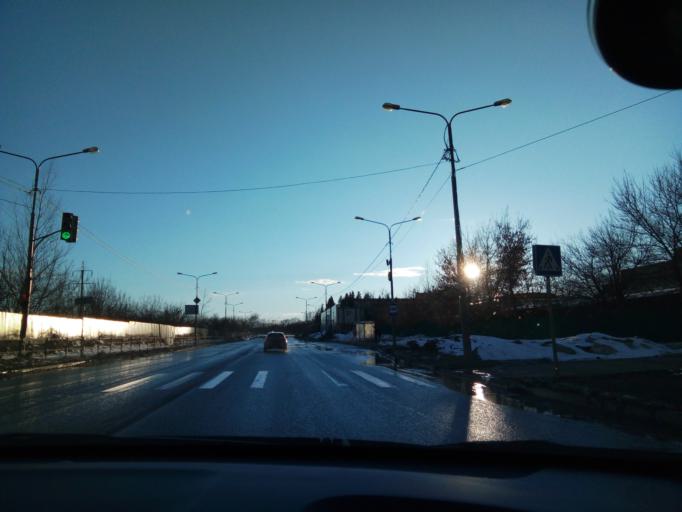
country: RU
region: Chuvashia
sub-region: Cheboksarskiy Rayon
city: Cheboksary
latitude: 56.1385
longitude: 47.2103
